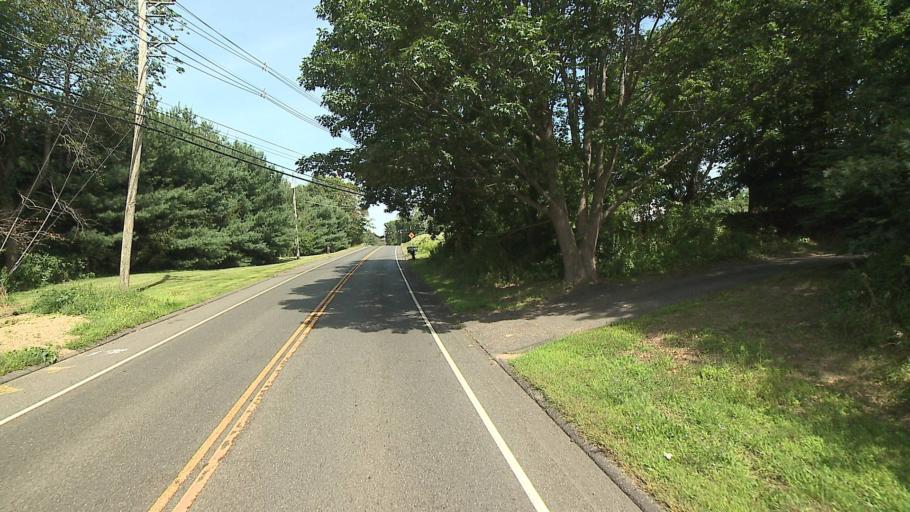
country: US
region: Connecticut
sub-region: Litchfield County
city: Oakville
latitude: 41.6093
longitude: -73.0920
